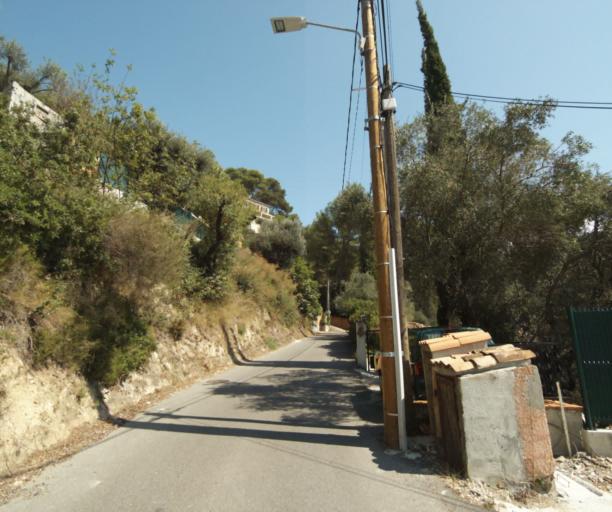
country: FR
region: Provence-Alpes-Cote d'Azur
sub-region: Departement des Alpes-Maritimes
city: Drap
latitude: 43.7551
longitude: 7.3322
